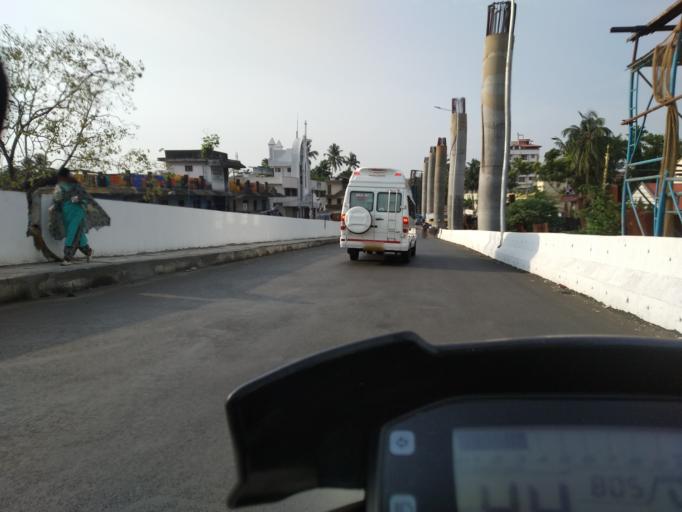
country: IN
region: Kerala
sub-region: Ernakulam
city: Cochin
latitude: 9.9559
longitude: 76.3272
